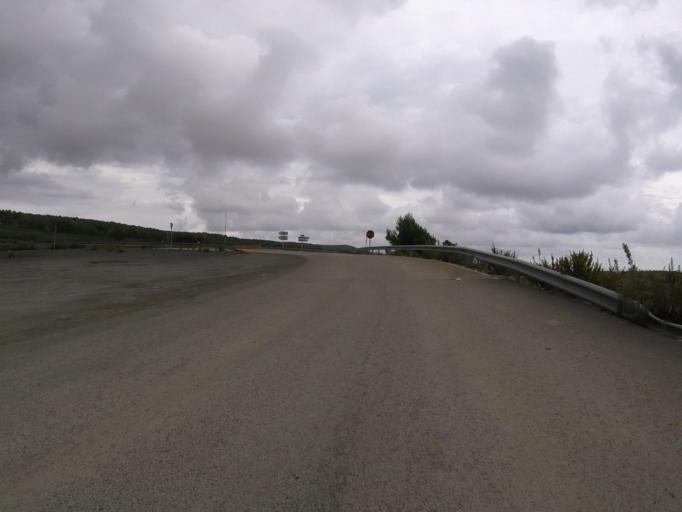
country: ES
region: Valencia
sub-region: Provincia de Castello
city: Benlloch
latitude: 40.2149
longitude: 0.0951
